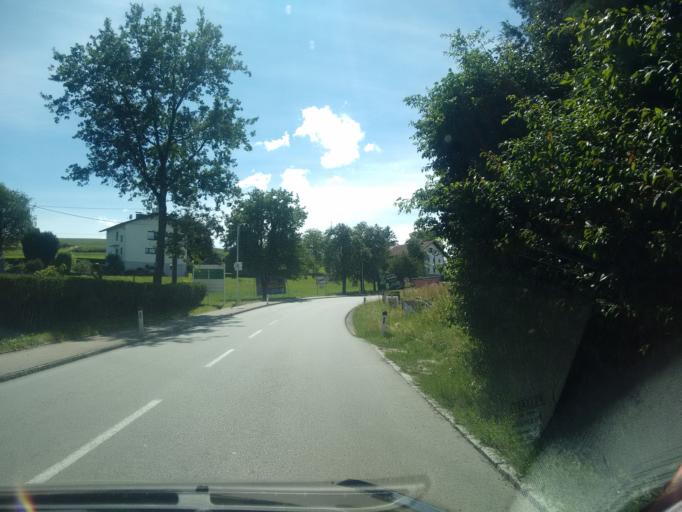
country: AT
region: Upper Austria
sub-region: Politischer Bezirk Ried im Innkreis
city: Ried im Innkreis
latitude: 48.2085
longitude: 13.4291
